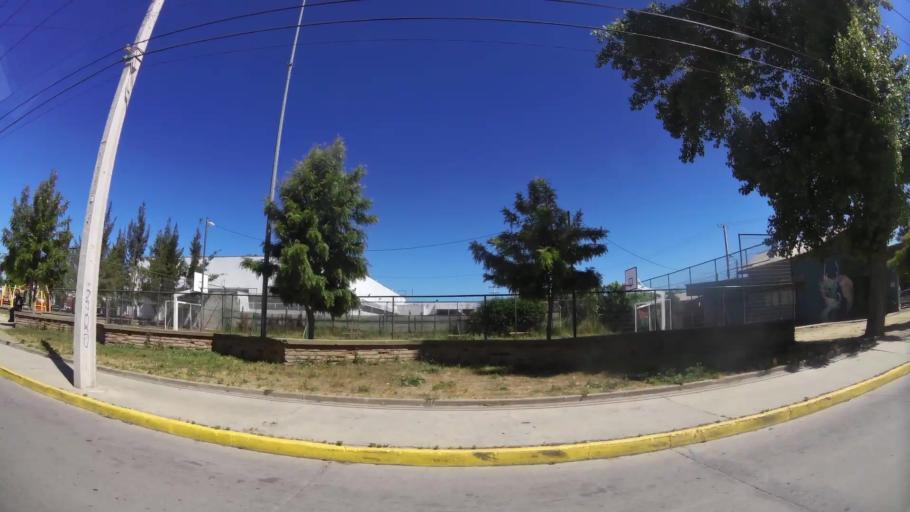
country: CL
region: Valparaiso
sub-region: Provincia de Marga Marga
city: Quilpue
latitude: -33.3228
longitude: -71.4043
